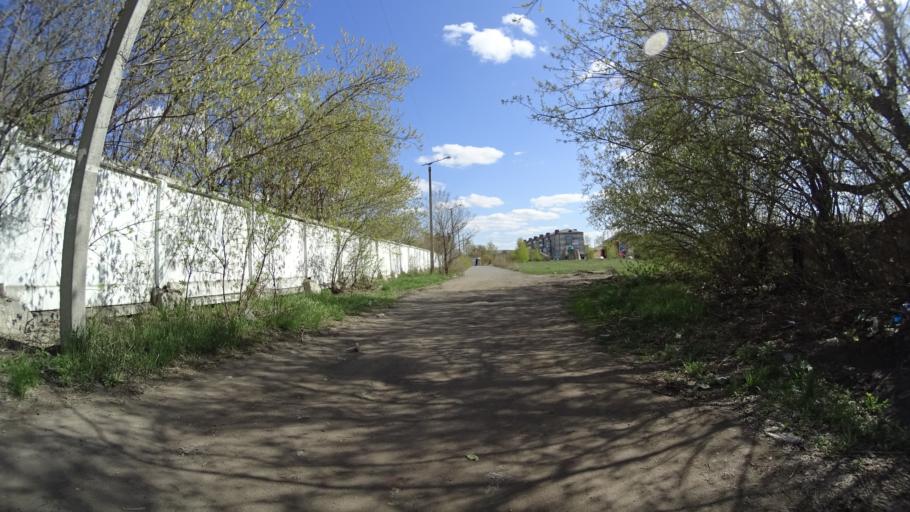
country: RU
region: Chelyabinsk
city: Troitsk
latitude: 54.0823
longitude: 61.5314
